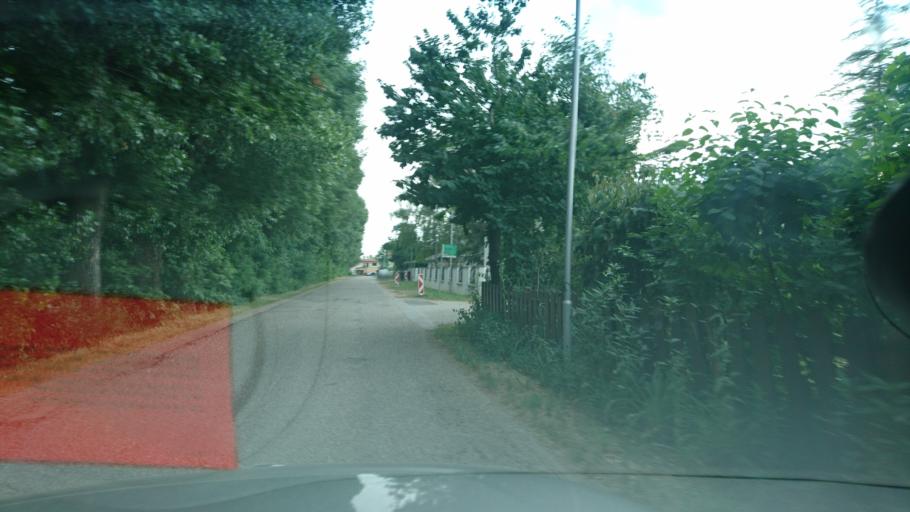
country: AT
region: Burgenland
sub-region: Politischer Bezirk Neusiedl am See
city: Neusiedl am See
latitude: 47.9363
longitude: 16.8532
